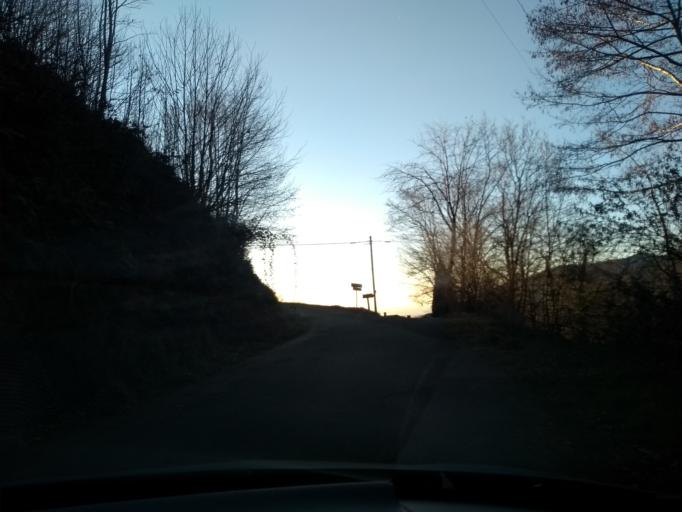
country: IT
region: Piedmont
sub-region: Provincia di Torino
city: Corio
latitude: 45.3241
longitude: 7.5394
